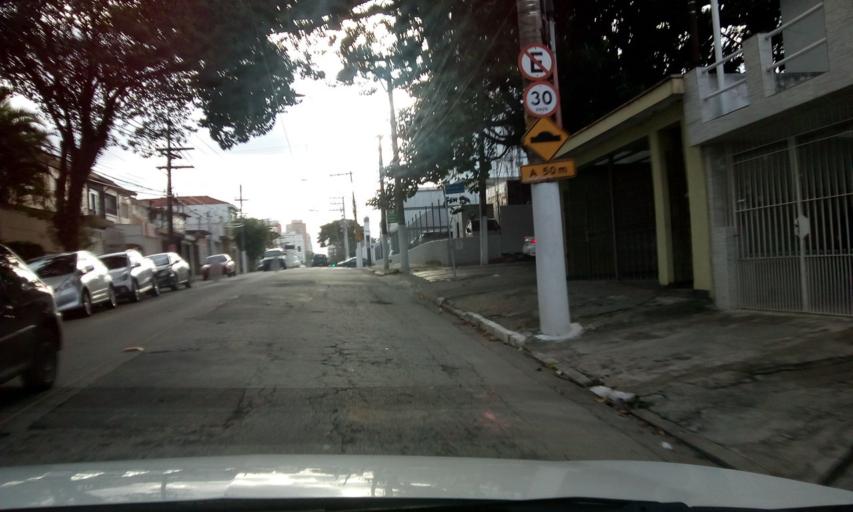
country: BR
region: Sao Paulo
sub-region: Sao Caetano Do Sul
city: Sao Caetano do Sul
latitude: -23.5433
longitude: -46.5541
